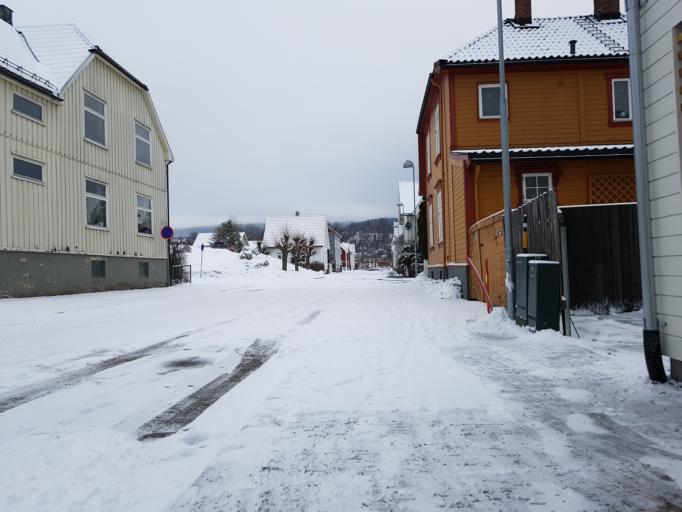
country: NO
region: Buskerud
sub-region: Drammen
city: Drammen
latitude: 59.7387
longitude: 10.1924
